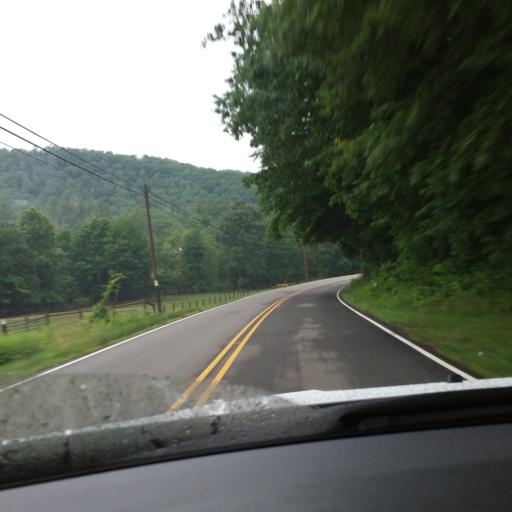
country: US
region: North Carolina
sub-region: Yancey County
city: Burnsville
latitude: 35.8169
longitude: -82.1923
